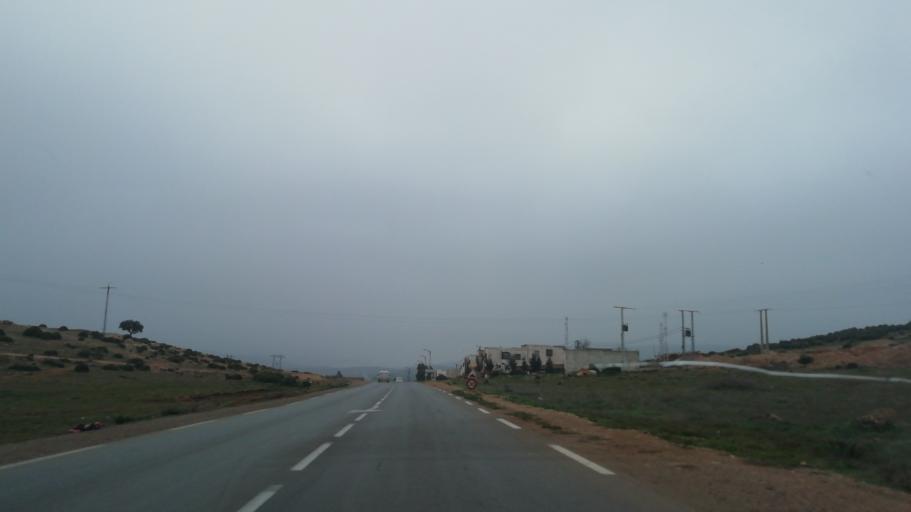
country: DZ
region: Mascara
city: Oued el Abtal
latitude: 35.2918
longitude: 0.4674
